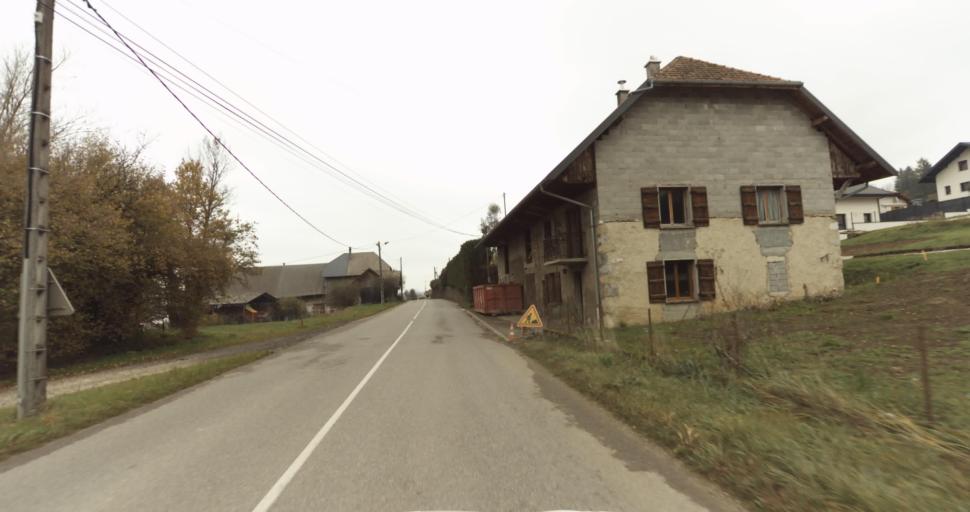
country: FR
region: Rhone-Alpes
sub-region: Departement de la Haute-Savoie
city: Viuz-la-Chiesaz
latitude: 45.8218
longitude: 6.0589
